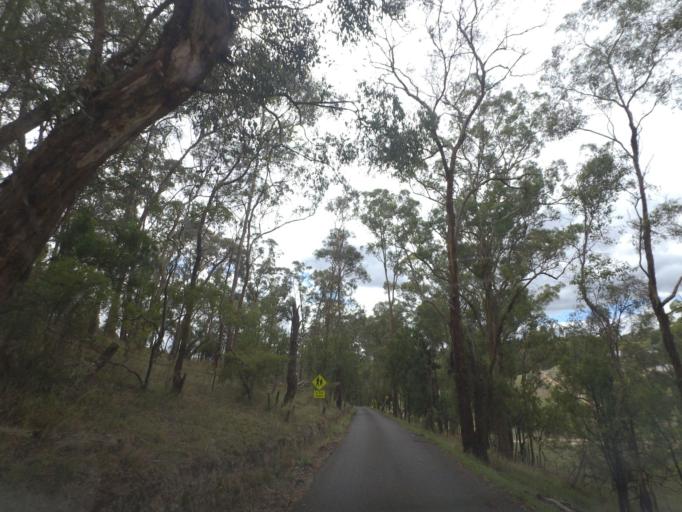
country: AU
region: Victoria
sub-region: Manningham
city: Park Orchards
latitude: -37.7804
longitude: 145.1980
